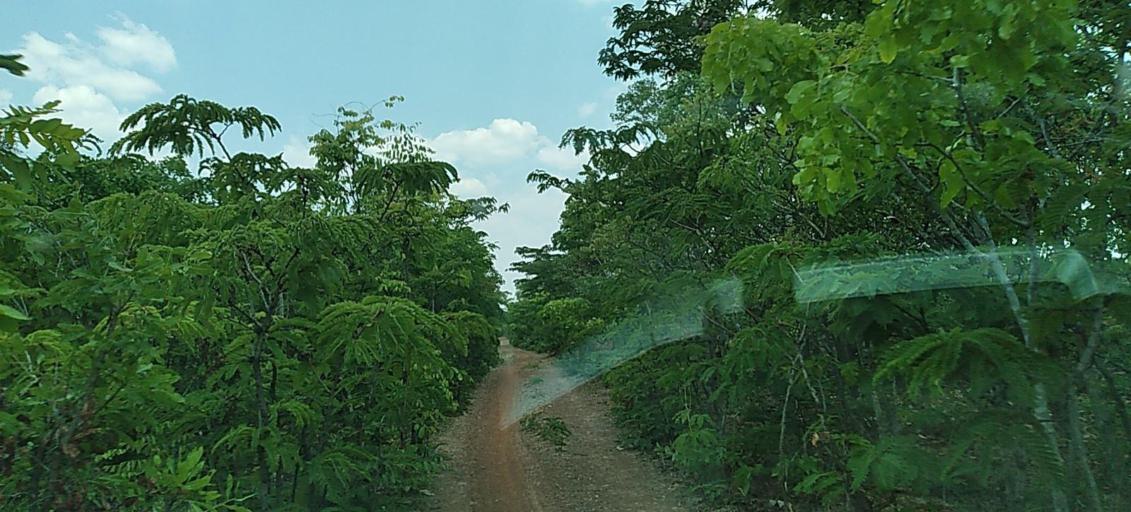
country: CD
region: Katanga
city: Kipushi
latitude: -12.0083
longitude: 27.4293
